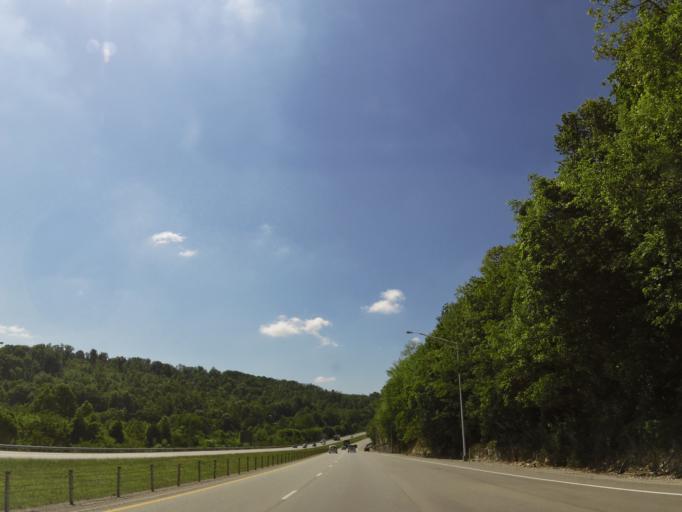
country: US
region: Kentucky
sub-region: Rockcastle County
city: Mount Vernon
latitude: 37.3392
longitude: -84.3073
